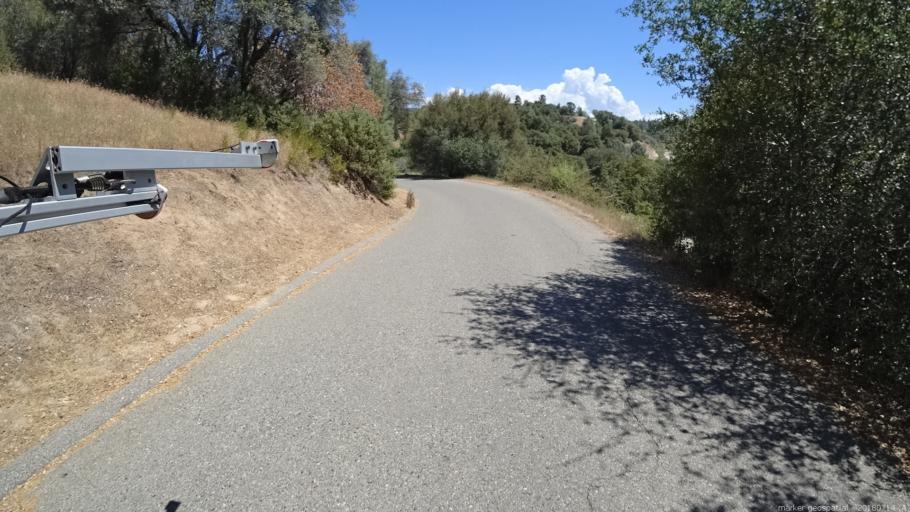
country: US
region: California
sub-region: Madera County
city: Oakhurst
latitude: 37.3654
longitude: -119.6573
